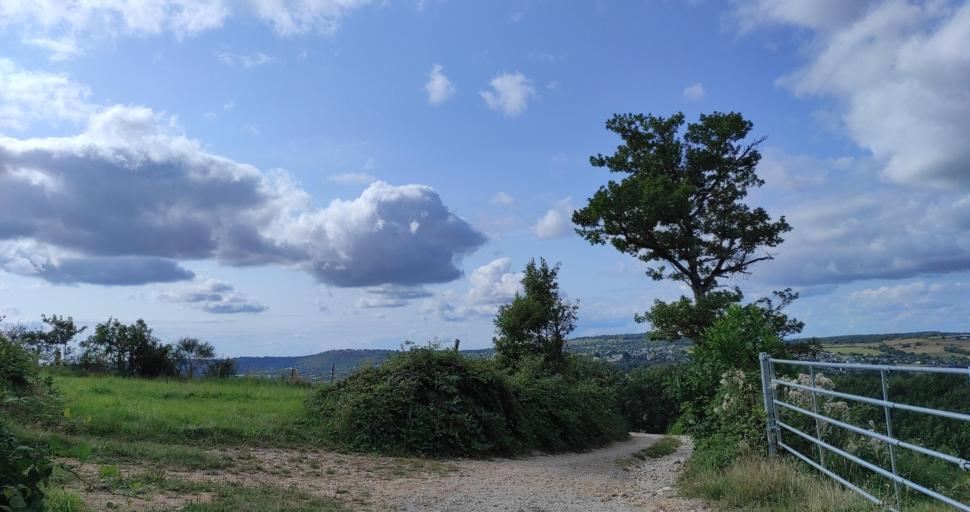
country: FR
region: Midi-Pyrenees
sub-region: Departement de l'Aveyron
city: La Loubiere
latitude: 44.3840
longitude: 2.7154
